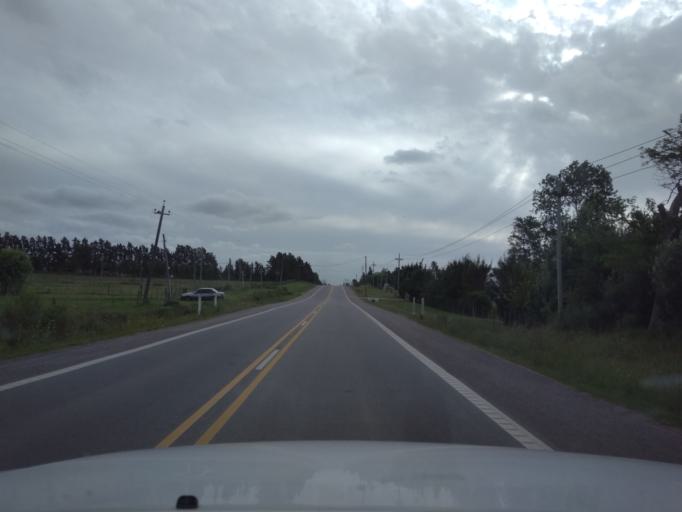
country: UY
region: Canelones
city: Joaquin Suarez
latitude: -34.7047
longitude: -56.0459
